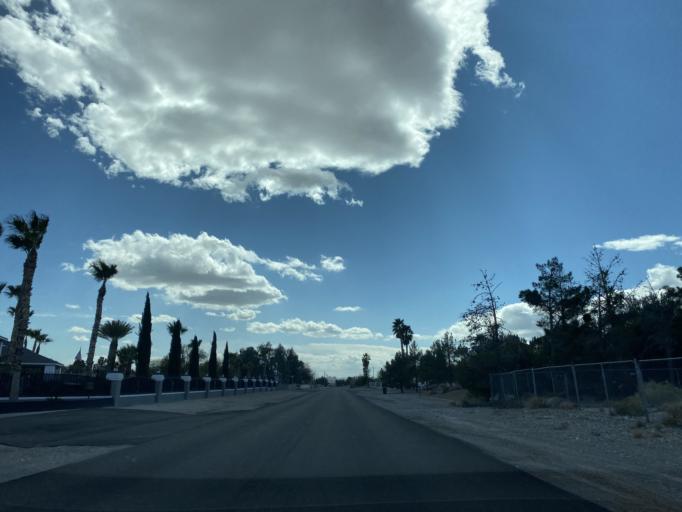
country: US
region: Nevada
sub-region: Clark County
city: Summerlin South
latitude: 36.2695
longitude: -115.2882
